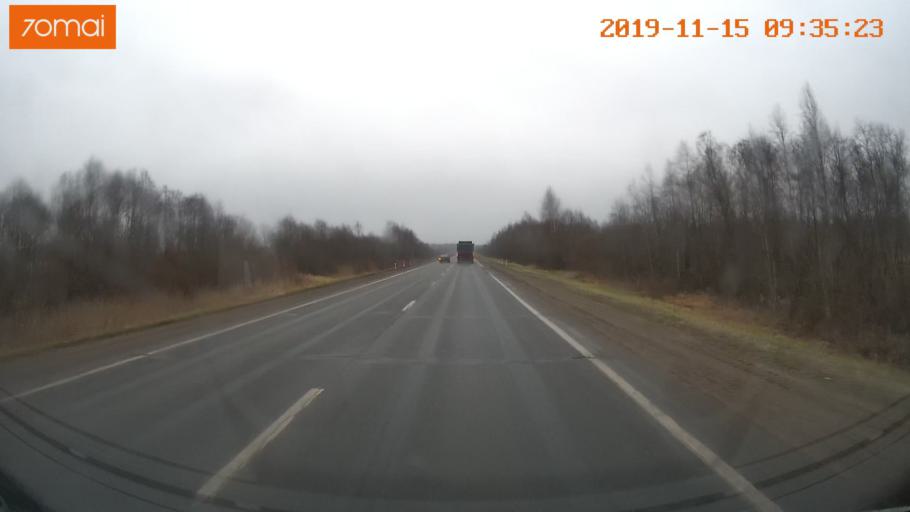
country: RU
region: Vologda
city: Sheksna
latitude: 59.2547
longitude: 38.3977
